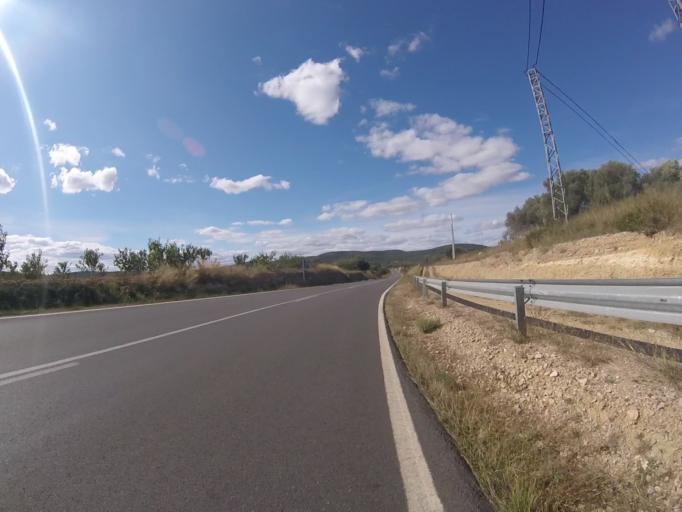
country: ES
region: Valencia
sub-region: Provincia de Castello
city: Chert/Xert
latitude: 40.4268
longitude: 0.1550
